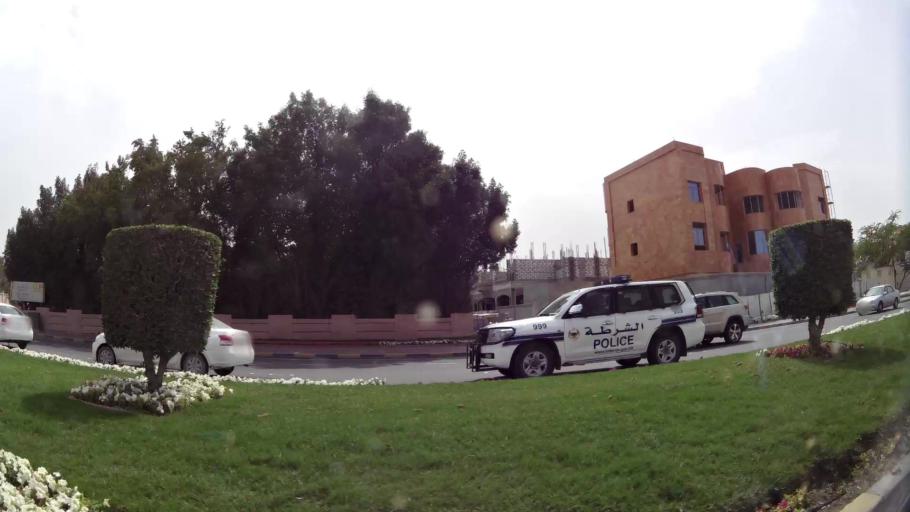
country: BH
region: Northern
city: Ar Rifa'
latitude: 26.1330
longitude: 50.5405
